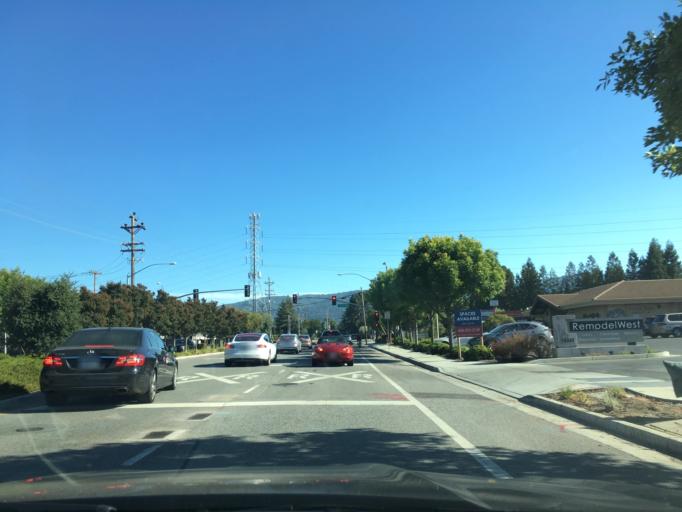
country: US
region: California
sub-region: Santa Clara County
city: Saratoga
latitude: 37.2898
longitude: -122.0325
